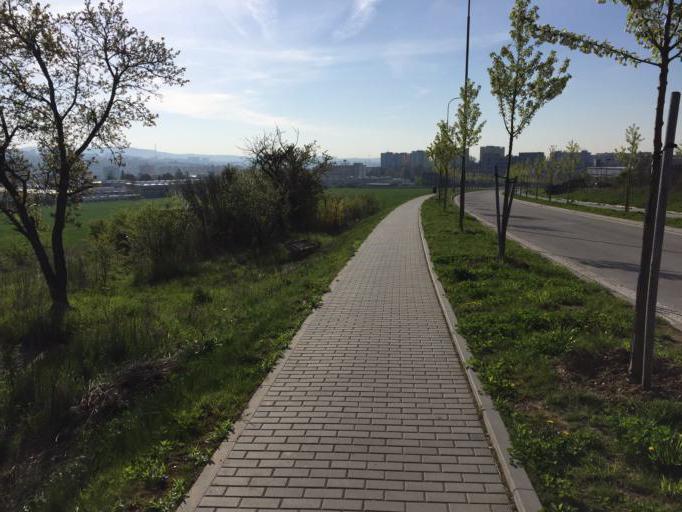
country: CZ
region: South Moravian
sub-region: Mesto Brno
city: Mokra Hora
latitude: 49.2353
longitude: 16.5731
